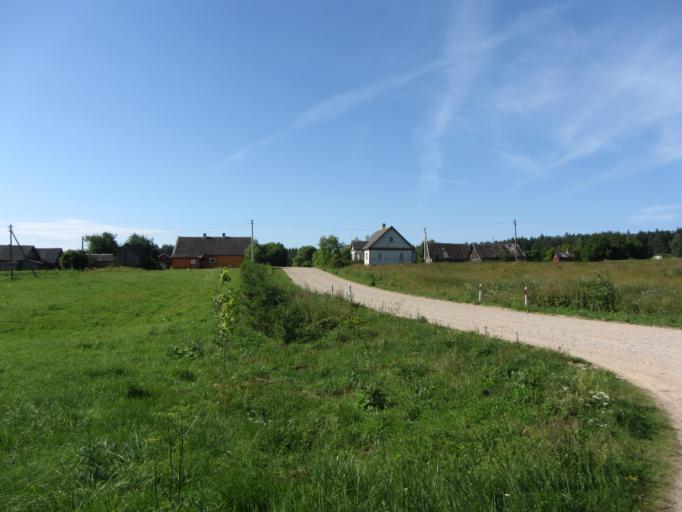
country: LT
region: Vilnius County
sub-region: Vilniaus Rajonas
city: Vievis
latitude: 54.8287
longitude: 24.8292
